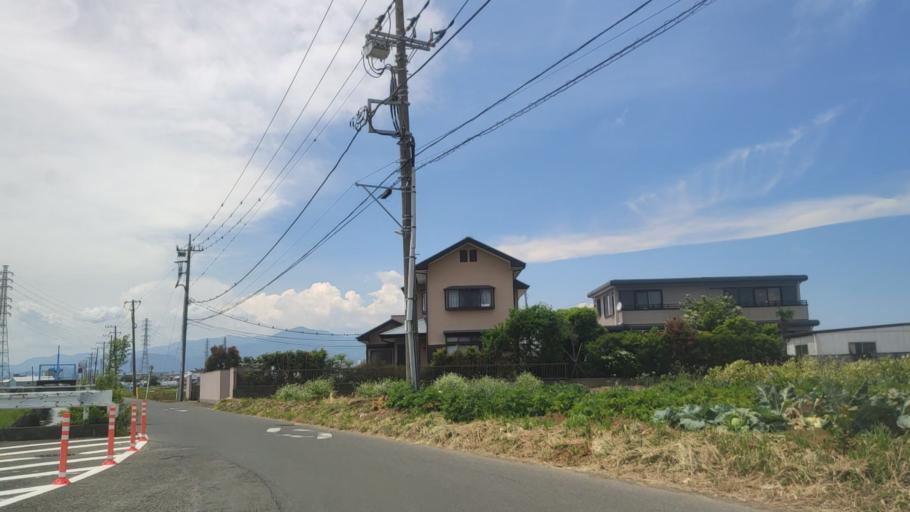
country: JP
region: Kanagawa
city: Chigasaki
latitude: 35.3560
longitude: 139.3908
